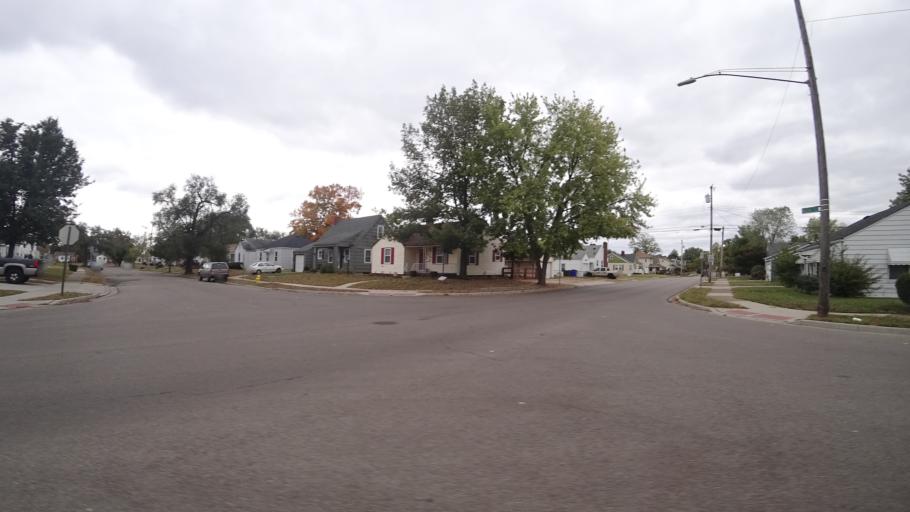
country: US
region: Ohio
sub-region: Butler County
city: Fairfield
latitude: 39.3699
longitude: -84.5624
